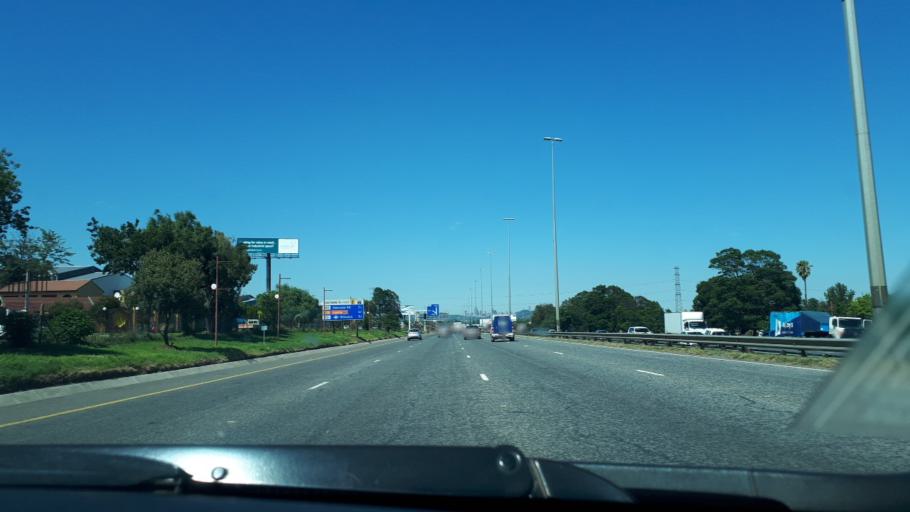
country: ZA
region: Gauteng
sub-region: City of Johannesburg Metropolitan Municipality
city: Modderfontein
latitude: -26.1430
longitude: 28.1877
